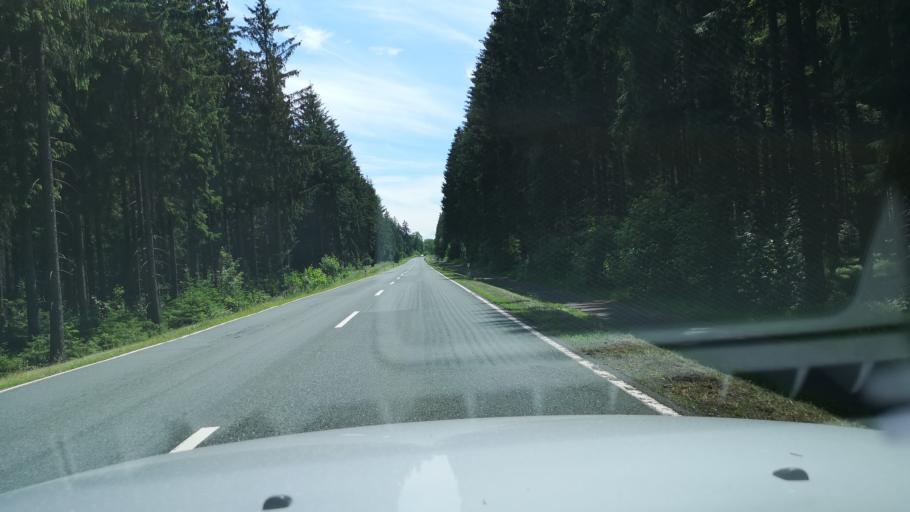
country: DE
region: Bavaria
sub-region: Upper Franconia
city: Ludwigsstadt
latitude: 50.4618
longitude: 11.3395
